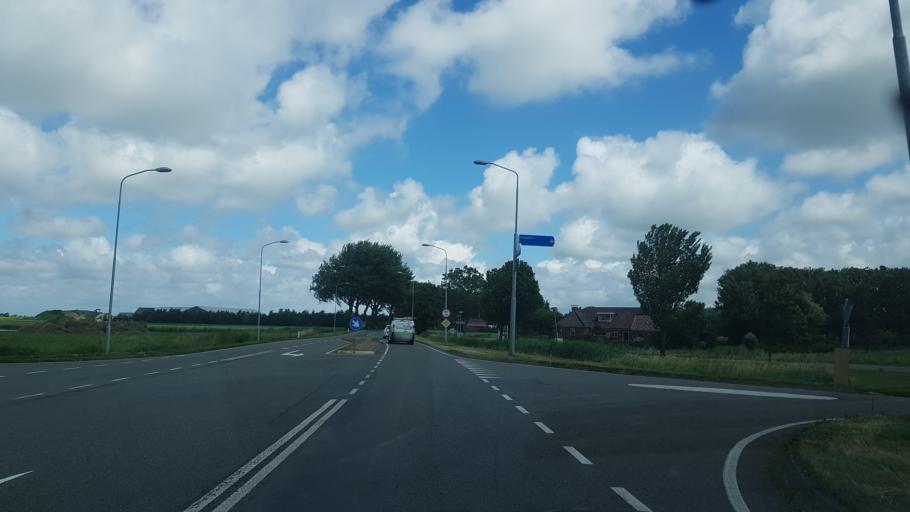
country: NL
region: Groningen
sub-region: Gemeente Bedum
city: Bedum
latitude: 53.4017
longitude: 6.5950
